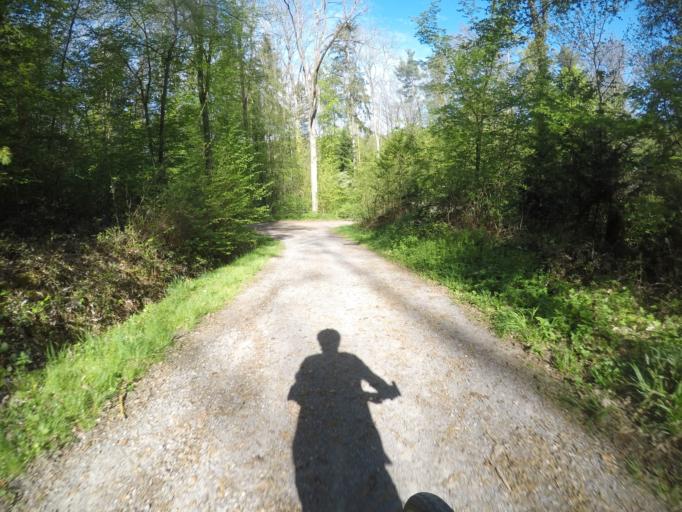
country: DE
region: Baden-Wuerttemberg
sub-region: Regierungsbezirk Stuttgart
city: Stuttgart
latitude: 48.7431
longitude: 9.1457
